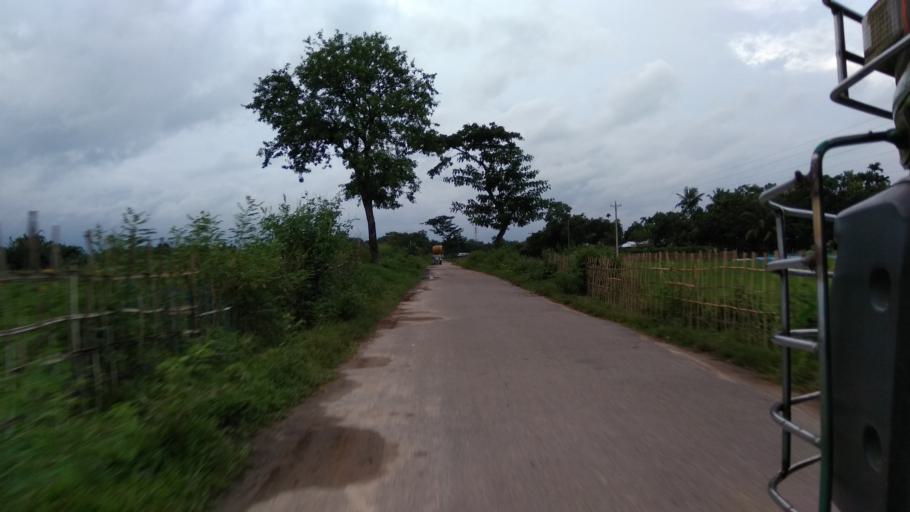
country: IN
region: Tripura
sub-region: Dhalai
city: Kamalpur
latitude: 24.2102
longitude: 91.8609
